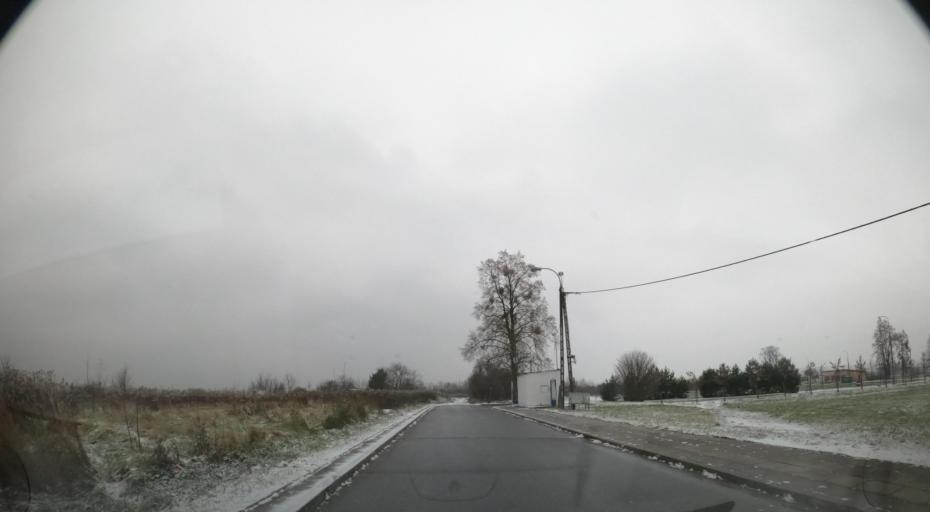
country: PL
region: Masovian Voivodeship
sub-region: Powiat plocki
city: Wyszogrod
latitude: 52.3845
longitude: 20.1827
